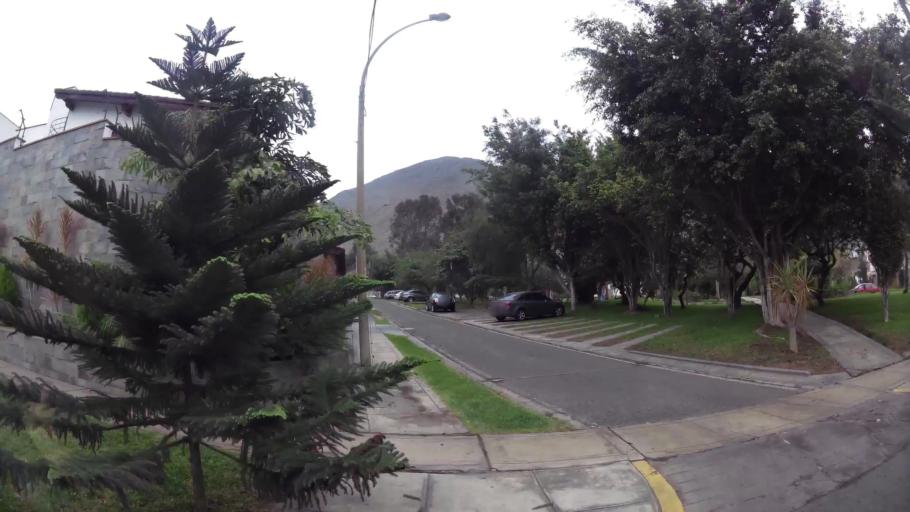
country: PE
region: Lima
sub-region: Lima
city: La Molina
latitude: -12.0959
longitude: -76.9253
